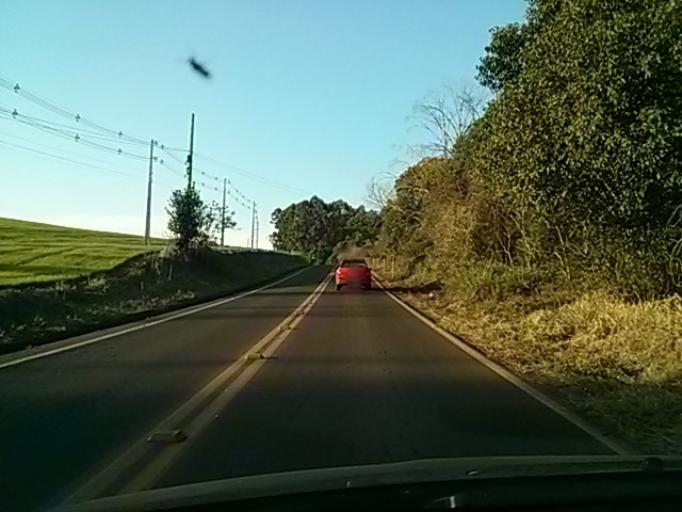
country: BR
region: Santa Catarina
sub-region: Chapeco
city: Chapeco
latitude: -27.1081
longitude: -52.7092
